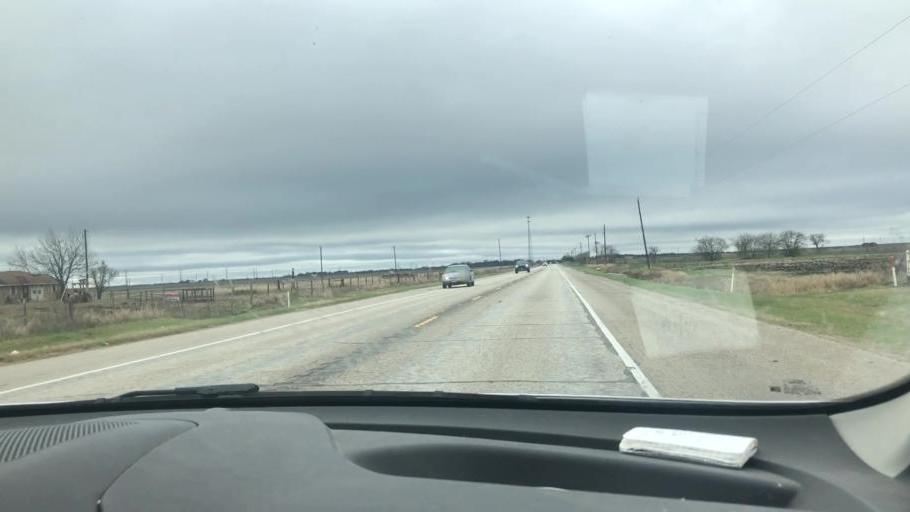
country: US
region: Texas
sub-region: Wharton County
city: Wharton
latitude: 29.2394
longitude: -96.0413
